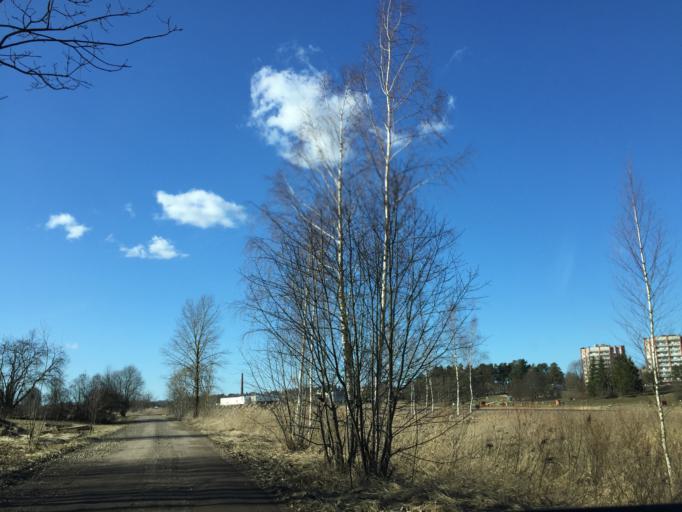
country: LV
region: Ogre
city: Ogre
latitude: 56.8116
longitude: 24.5940
